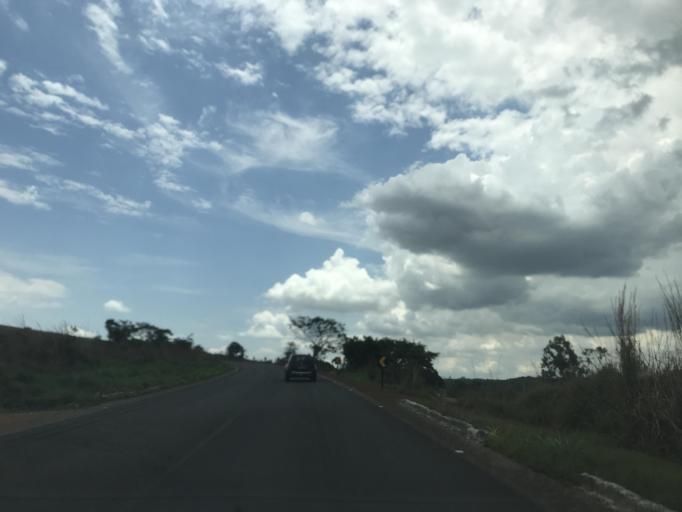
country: BR
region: Goias
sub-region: Vianopolis
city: Vianopolis
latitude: -16.9470
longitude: -48.5860
